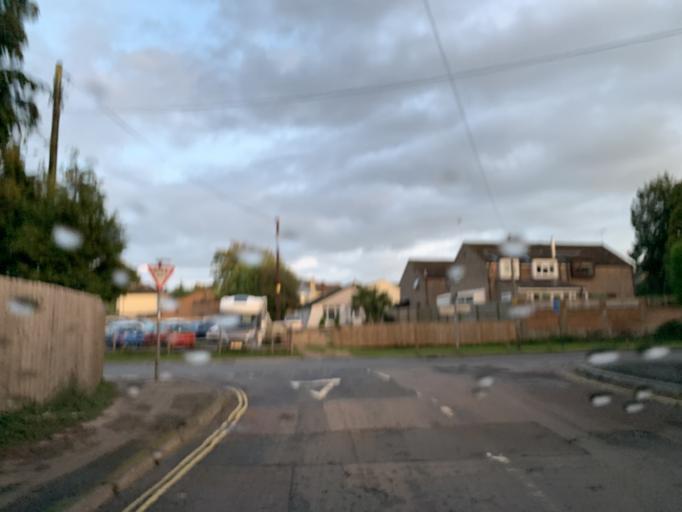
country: GB
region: England
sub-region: Hampshire
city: Brockenhurst
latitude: 50.8176
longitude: -1.5774
